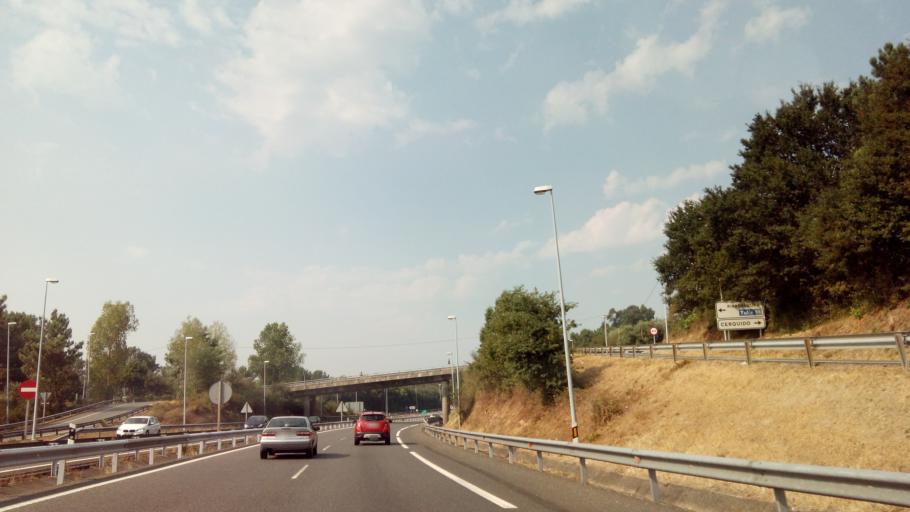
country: ES
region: Galicia
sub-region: Provincia de Pontevedra
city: Tui
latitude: 42.0928
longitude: -8.6269
